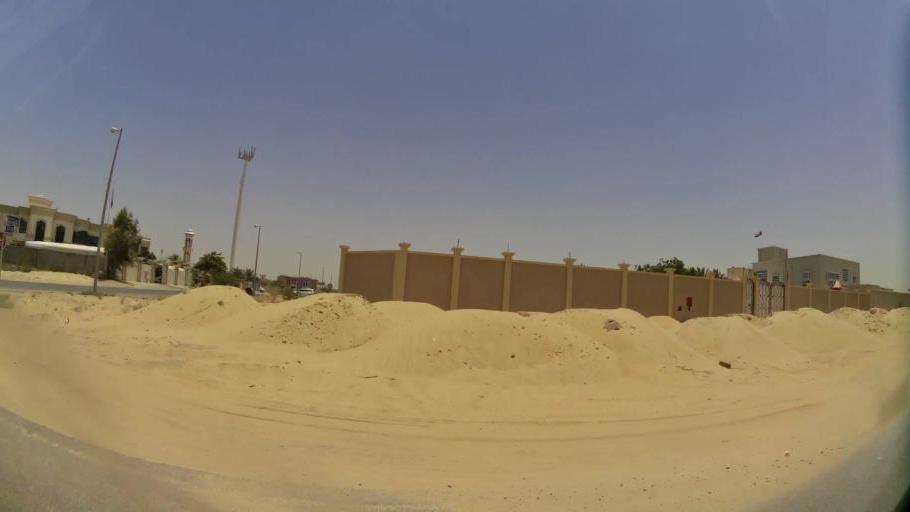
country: AE
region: Ajman
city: Ajman
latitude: 25.4118
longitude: 55.4921
